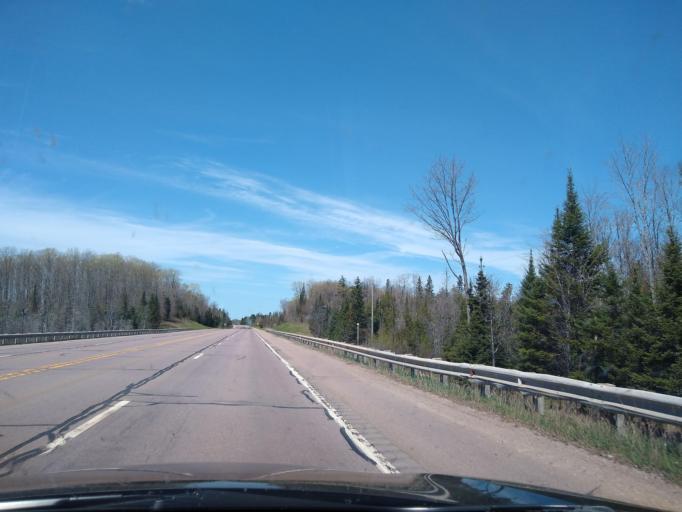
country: US
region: Michigan
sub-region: Marquette County
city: K. I. Sawyer Air Force Base
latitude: 46.2633
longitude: -87.1008
